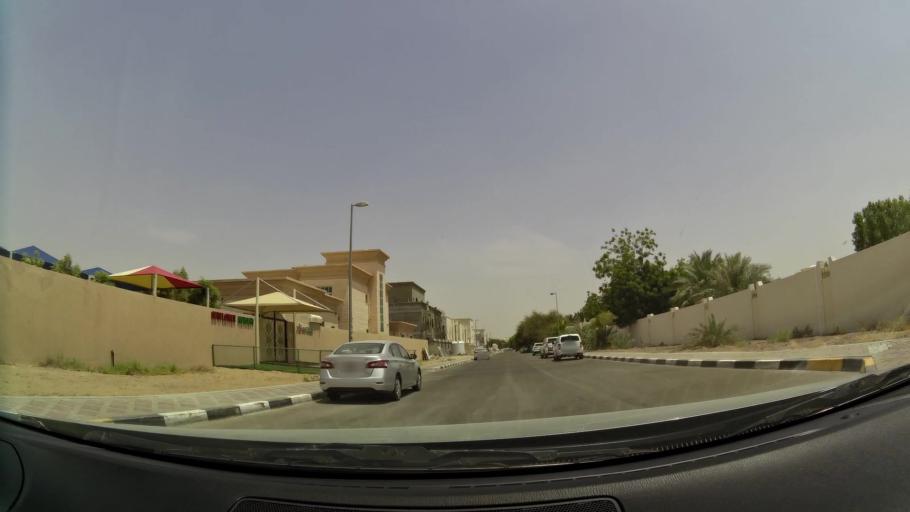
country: AE
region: Abu Dhabi
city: Al Ain
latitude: 24.1858
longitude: 55.7326
